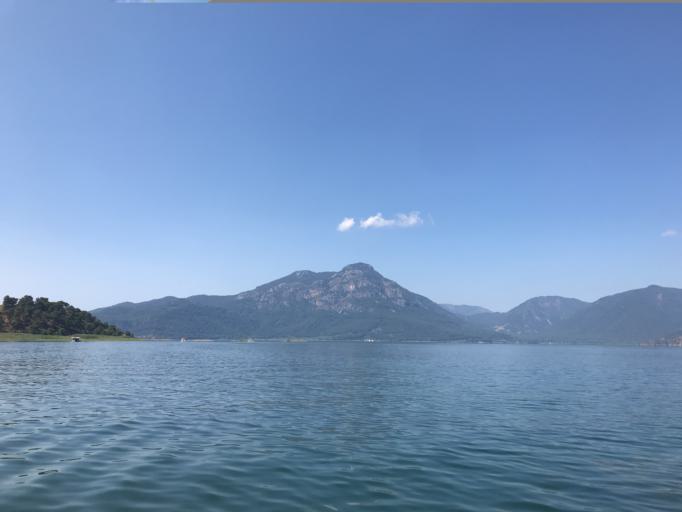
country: TR
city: Dalyan
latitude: 36.9018
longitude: 28.6459
